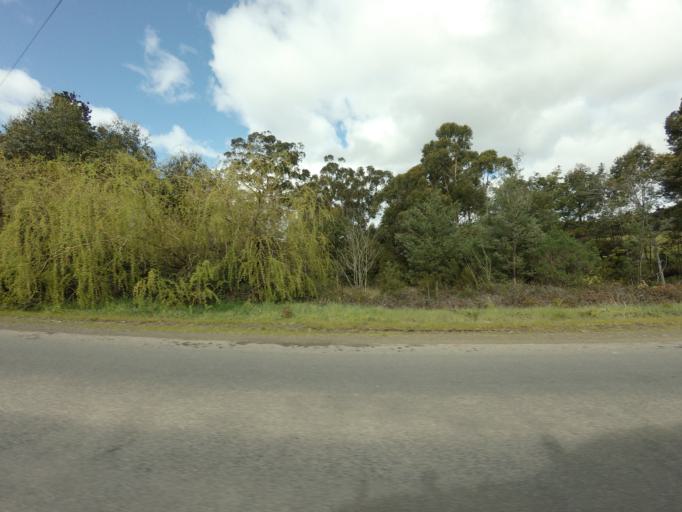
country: AU
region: Tasmania
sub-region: Huon Valley
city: Geeveston
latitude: -43.1920
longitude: 146.9590
